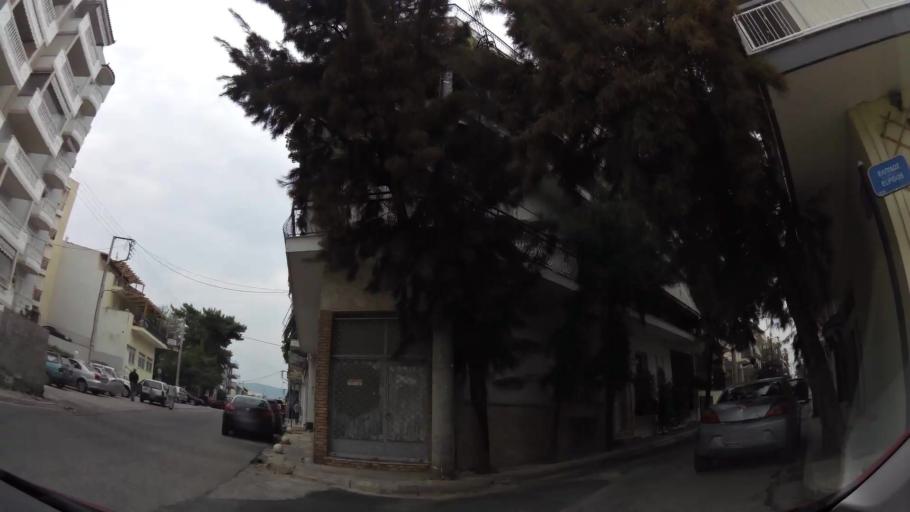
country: GR
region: Attica
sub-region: Nomarchia Athinas
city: Ilion
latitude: 38.0213
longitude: 23.7041
